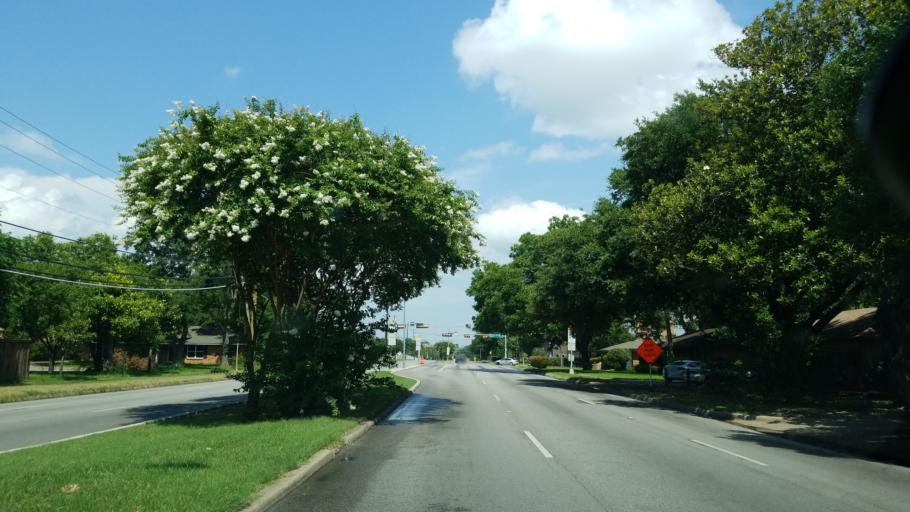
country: US
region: Texas
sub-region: Dallas County
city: Farmers Branch
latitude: 32.8809
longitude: -96.8672
